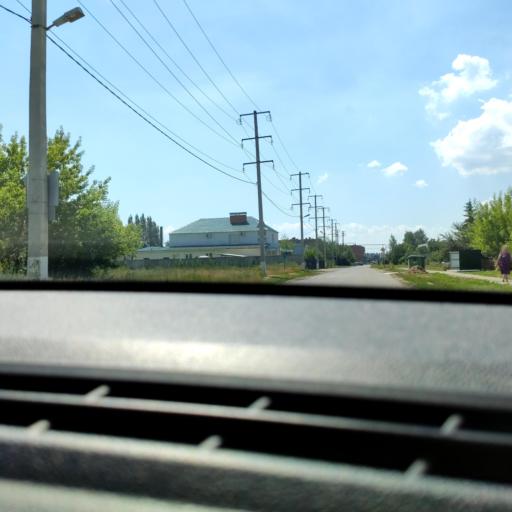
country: RU
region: Samara
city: Podstepki
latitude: 53.5176
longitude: 49.1126
